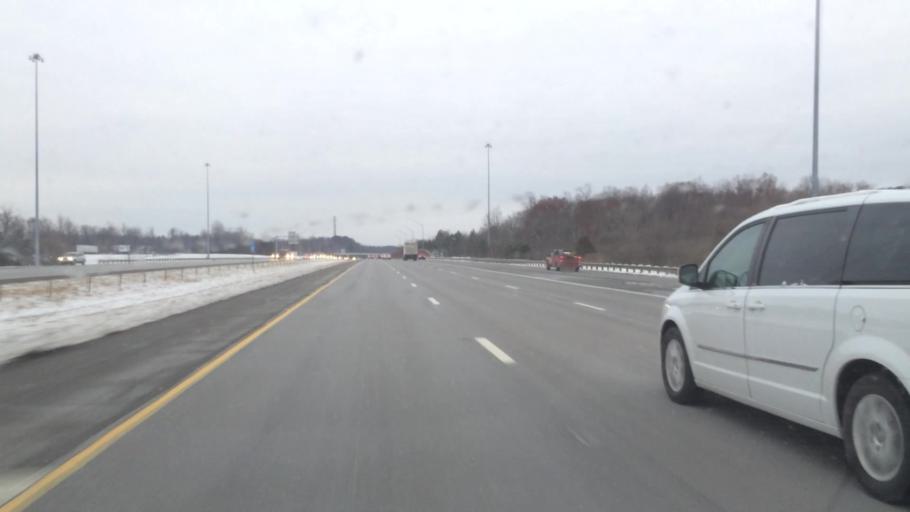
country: US
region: Ohio
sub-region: Medina County
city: Brunswick
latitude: 41.2362
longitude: -81.7976
